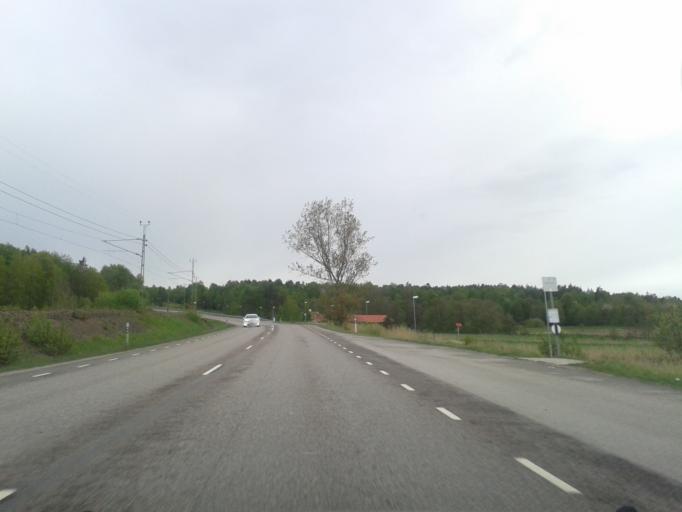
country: SE
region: Vaestra Goetaland
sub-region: Stenungsunds Kommun
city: Stora Hoga
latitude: 58.0023
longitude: 11.8271
